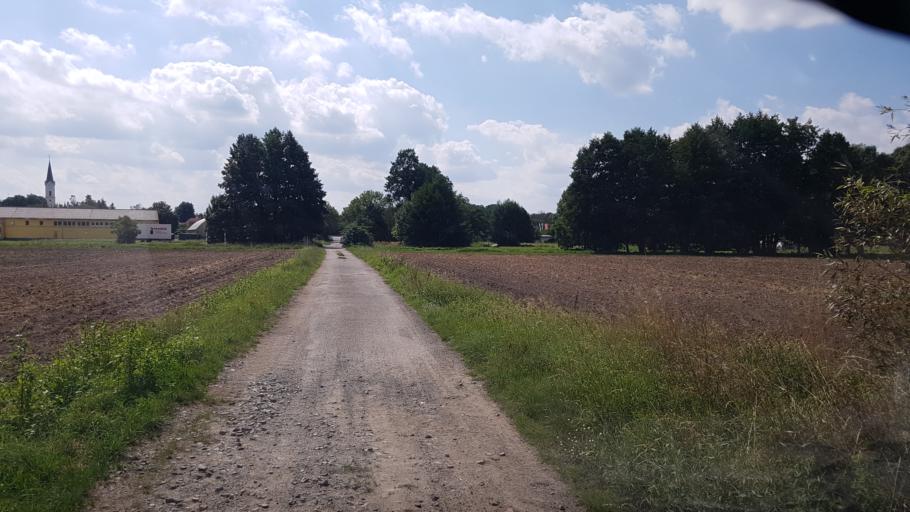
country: DE
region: Brandenburg
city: Lubbenau
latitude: 51.8673
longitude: 13.9278
